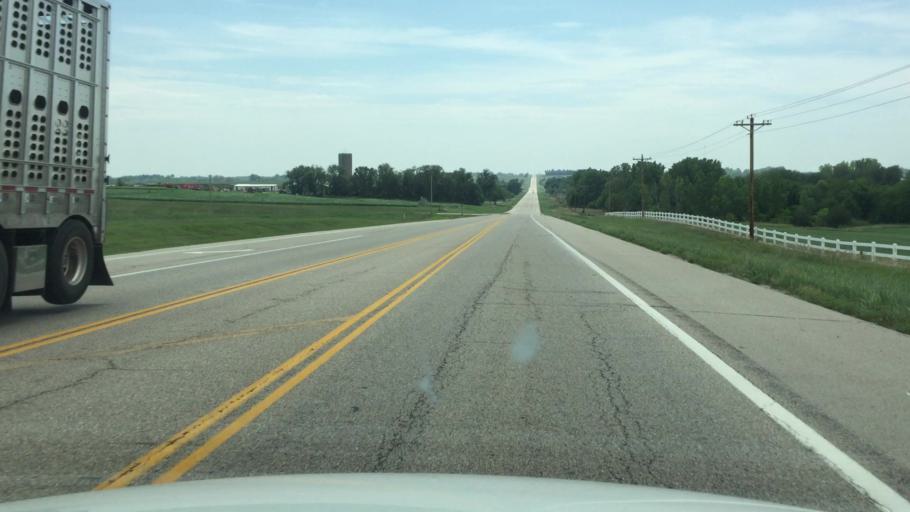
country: US
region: Kansas
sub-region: Brown County
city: Horton
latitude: 39.6988
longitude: -95.7303
